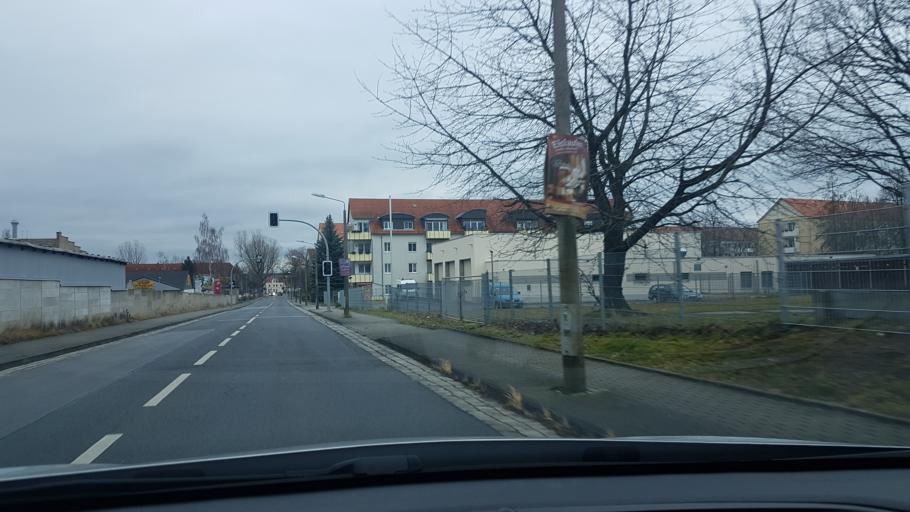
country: DE
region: Saxony
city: Goerlitz
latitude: 51.1241
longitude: 14.9756
